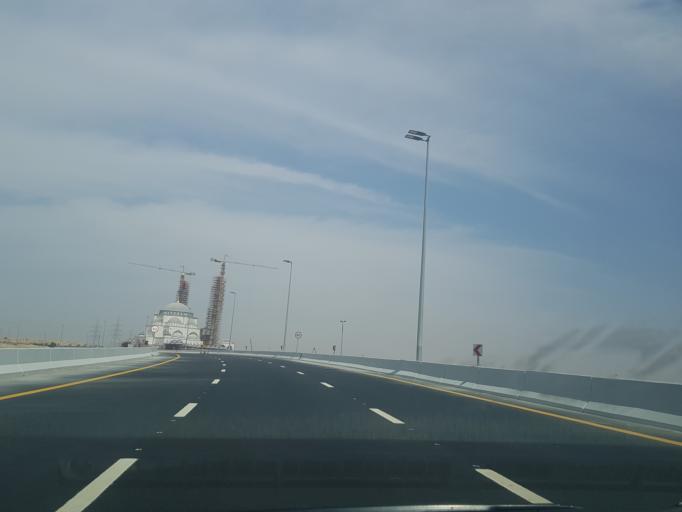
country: AE
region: Ash Shariqah
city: Sharjah
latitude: 25.2364
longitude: 55.5687
